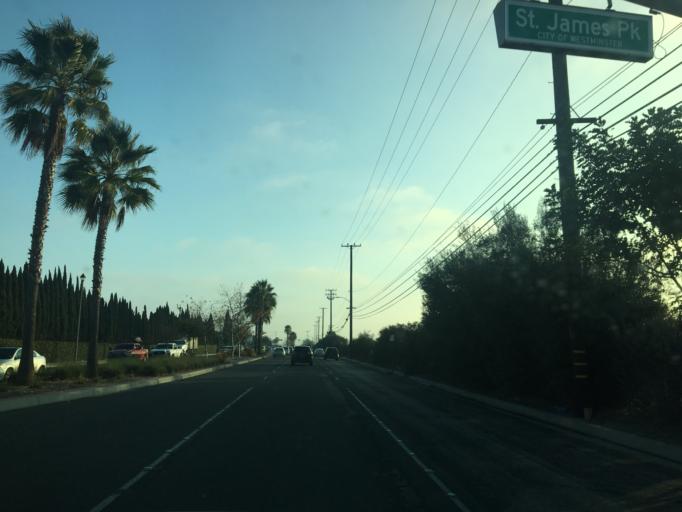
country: US
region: California
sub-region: Orange County
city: Westminster
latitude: 33.7564
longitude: -118.0427
